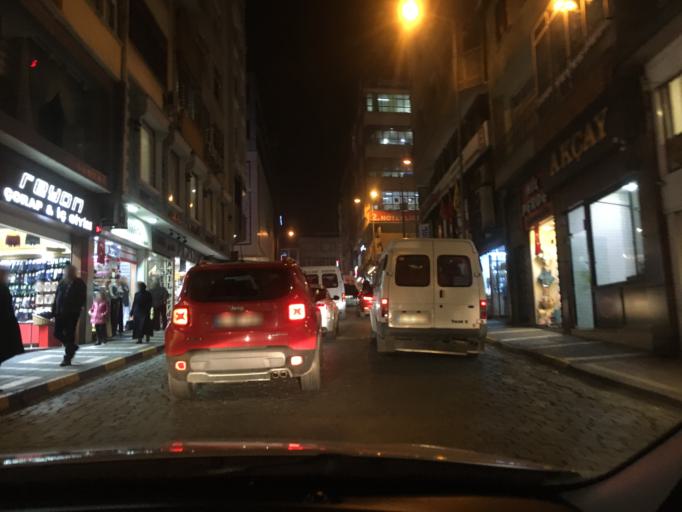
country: TR
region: Trabzon
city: Trabzon
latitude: 41.0067
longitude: 39.7257
